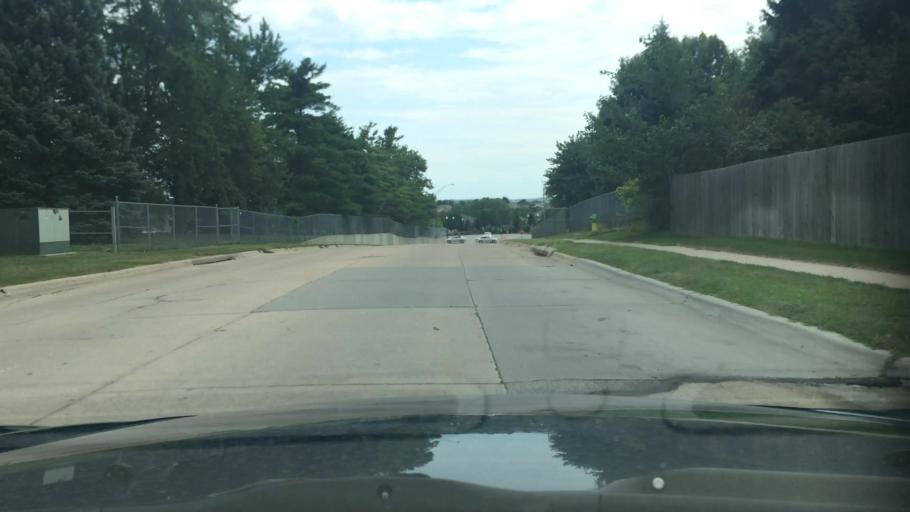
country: US
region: Nebraska
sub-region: Douglas County
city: Ralston
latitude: 41.1924
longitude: -96.0669
